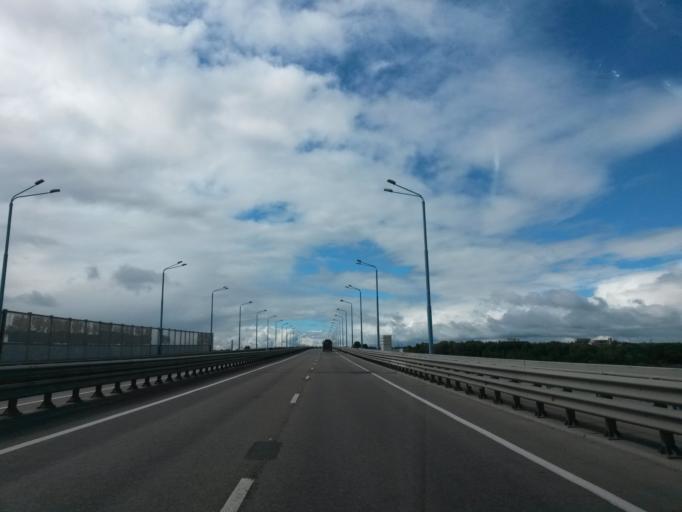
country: RU
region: Jaroslavl
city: Yaroslavl
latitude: 57.6764
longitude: 39.8611
